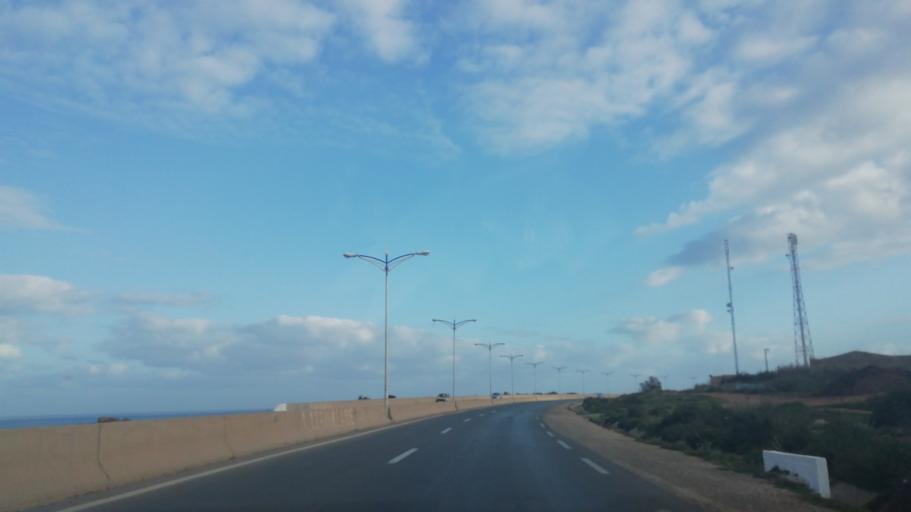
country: DZ
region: Mostaganem
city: Mostaganem
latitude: 36.0459
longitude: 0.1460
